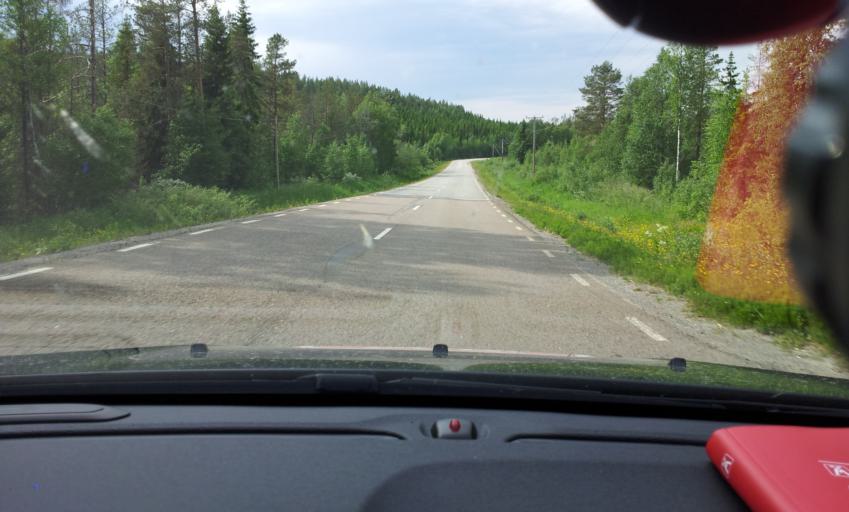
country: SE
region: Jaemtland
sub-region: OEstersunds Kommun
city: Brunflo
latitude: 62.6559
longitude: 14.8820
